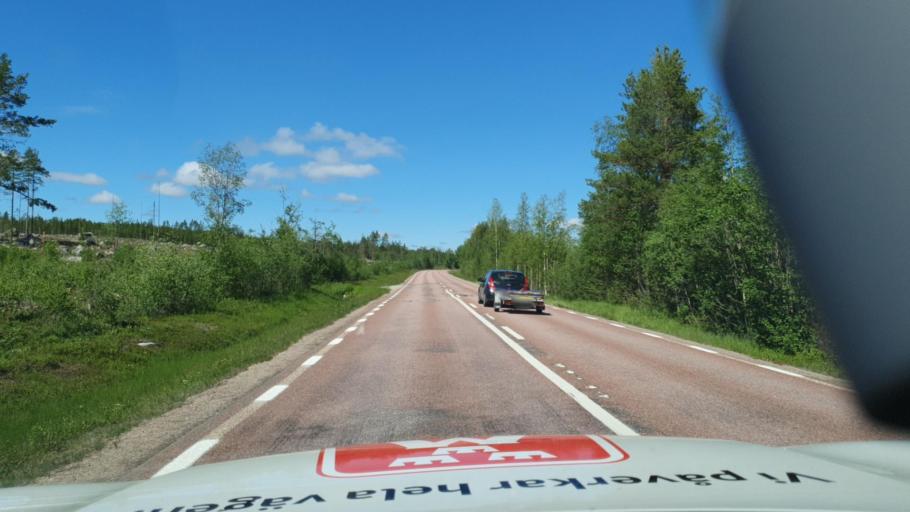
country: SE
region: Jaemtland
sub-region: Harjedalens Kommun
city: Sveg
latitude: 61.9532
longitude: 14.5806
